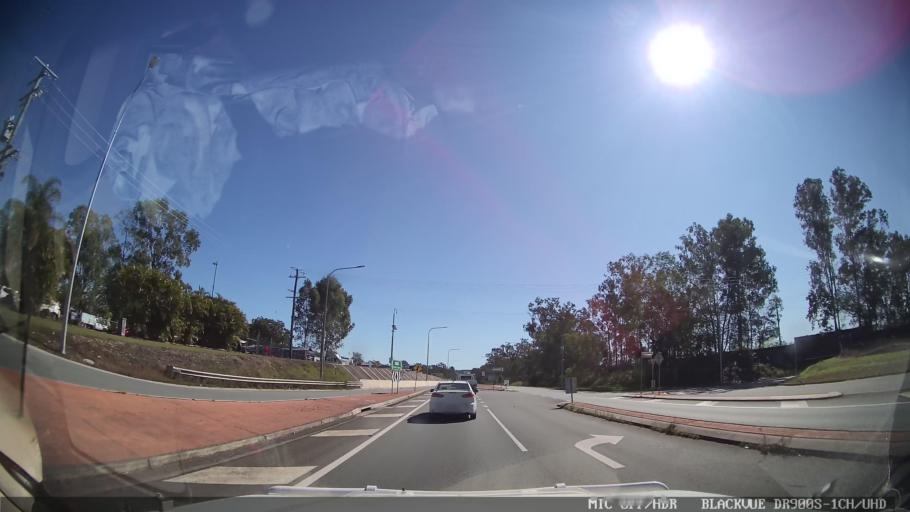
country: AU
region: Queensland
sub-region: Gympie Regional Council
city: Monkland
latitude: -26.2380
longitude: 152.6994
